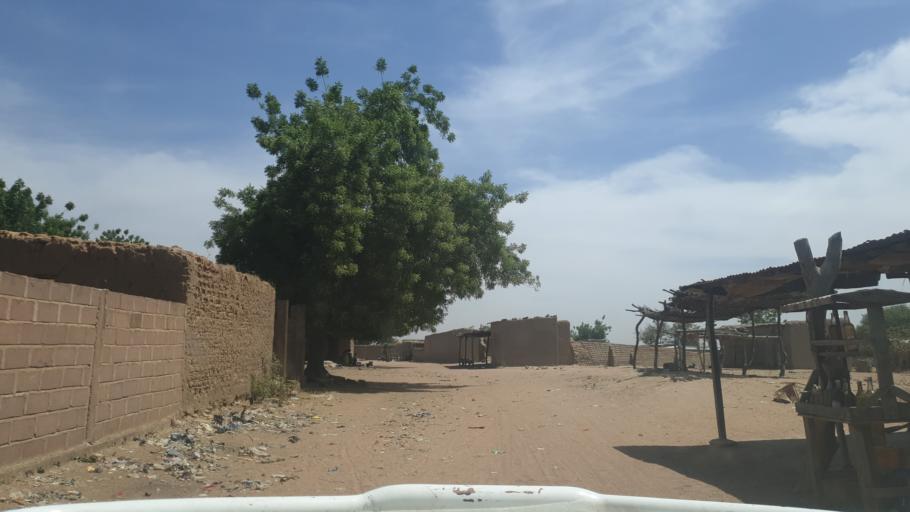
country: ML
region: Sikasso
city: Yorosso
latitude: 12.2914
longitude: -4.6490
